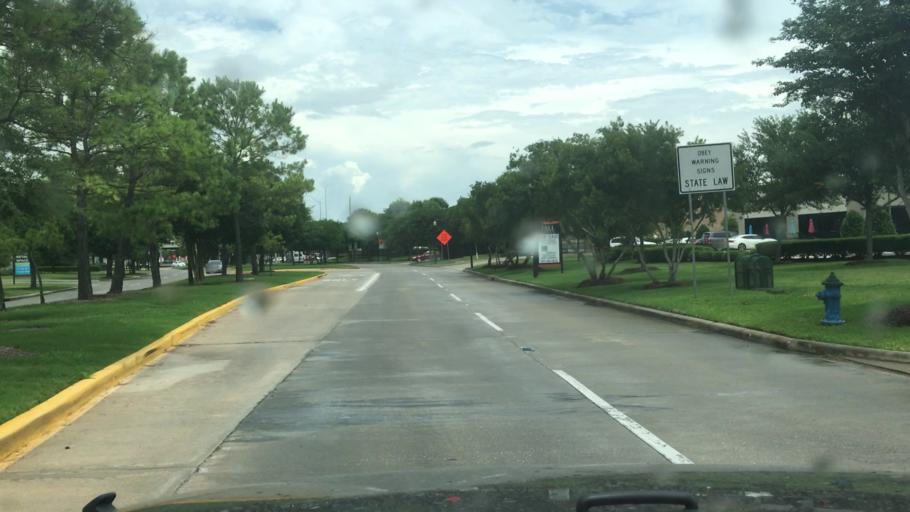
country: US
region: Texas
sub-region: Harris County
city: Humble
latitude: 29.9322
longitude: -95.2498
